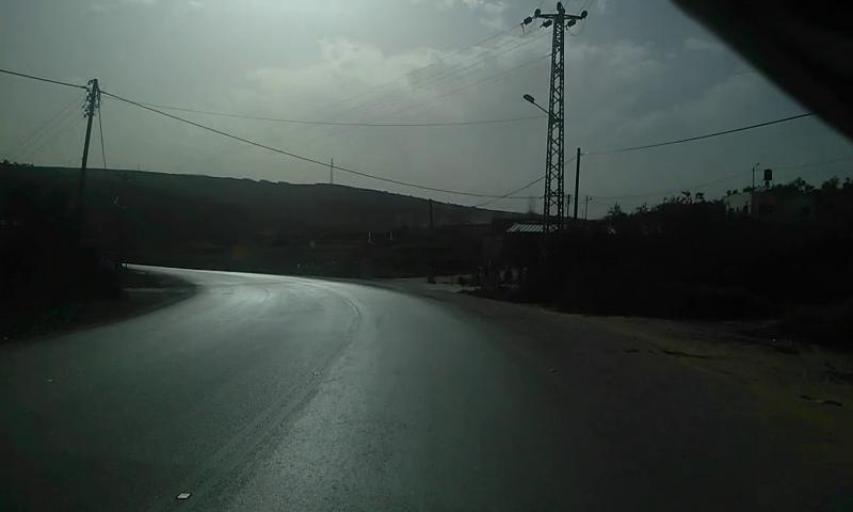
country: PS
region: West Bank
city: Dayr Sharaf
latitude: 32.2550
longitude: 35.1814
